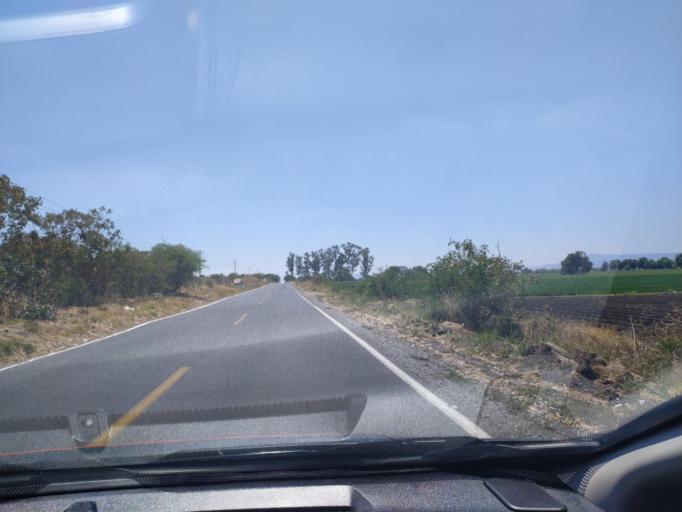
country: MX
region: Guanajuato
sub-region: San Francisco del Rincon
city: San Ignacio de Hidalgo
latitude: 20.8740
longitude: -101.8598
